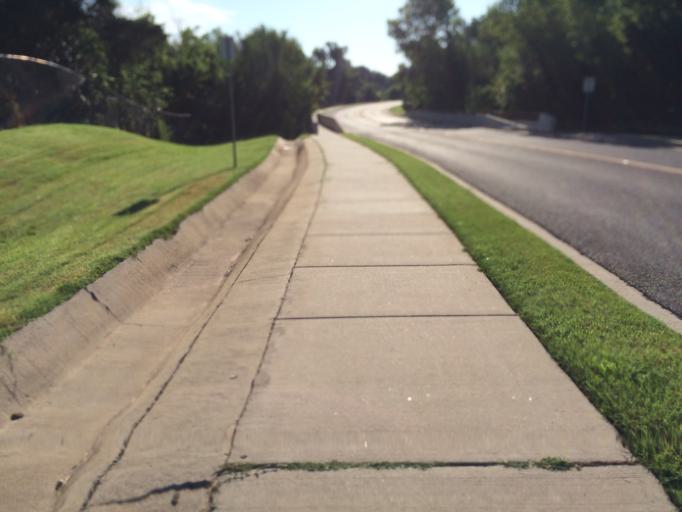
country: US
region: Oklahoma
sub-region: Cleveland County
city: Norman
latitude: 35.1914
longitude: -97.4306
